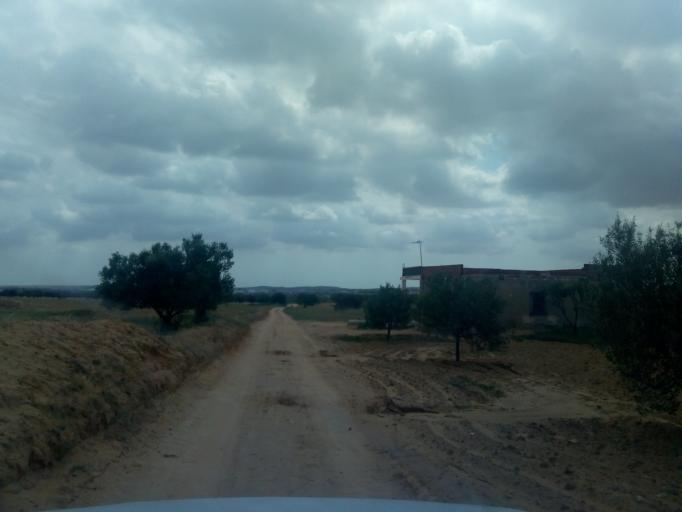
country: TN
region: Safaqis
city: Sfax
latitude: 34.7446
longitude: 10.4910
